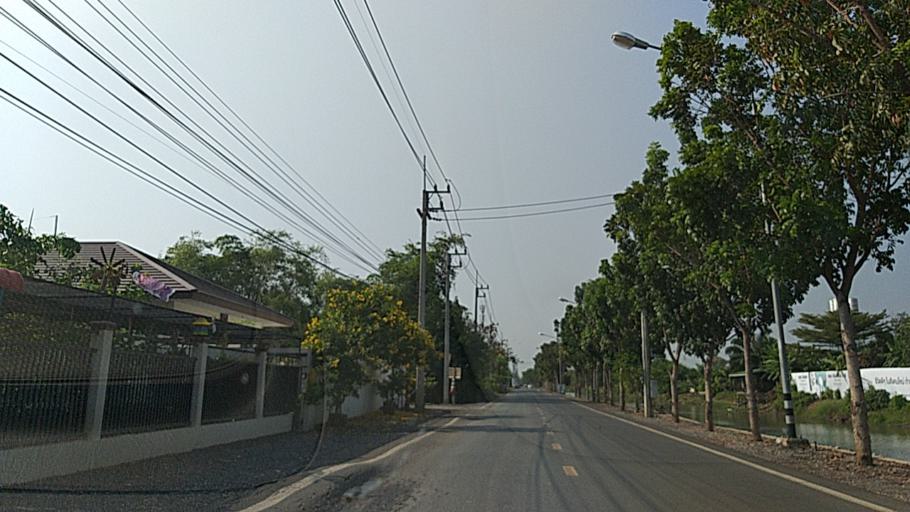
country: TH
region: Pathum Thani
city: Thanyaburi
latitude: 13.9861
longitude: 100.7059
